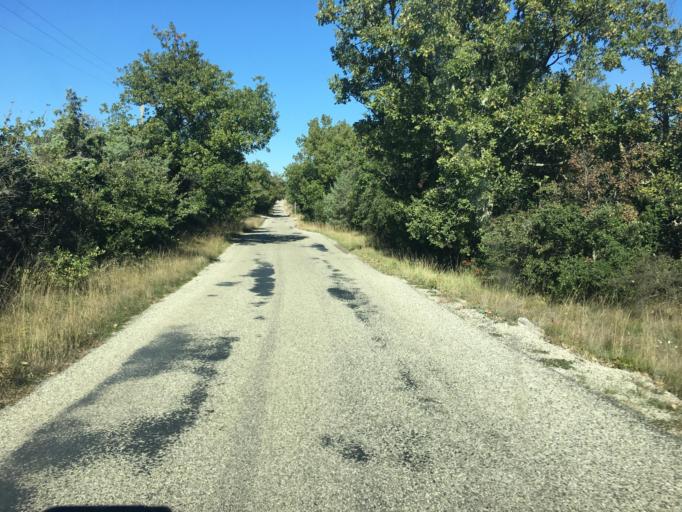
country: FR
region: Languedoc-Roussillon
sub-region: Departement du Gard
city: Montaren-et-Saint-Mediers
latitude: 44.1434
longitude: 4.3109
